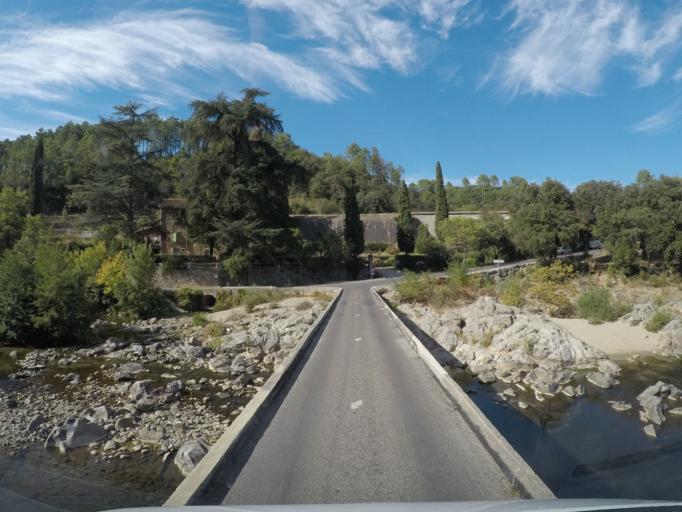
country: FR
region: Languedoc-Roussillon
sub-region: Departement du Gard
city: Anduze
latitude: 44.0749
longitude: 3.9625
